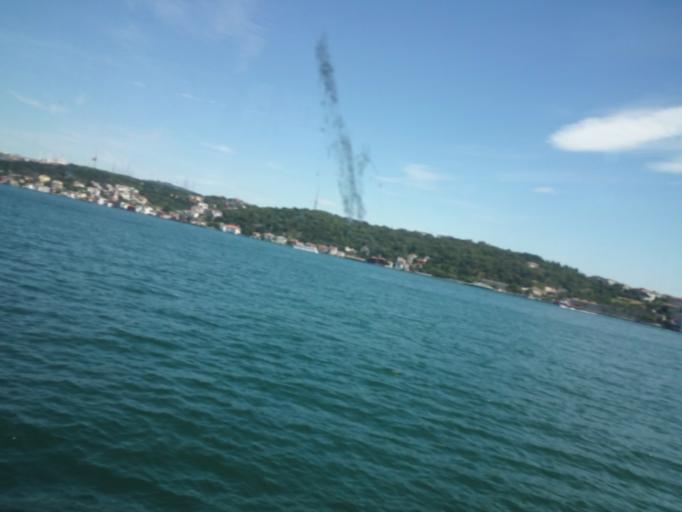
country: TR
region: Istanbul
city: UEskuedar
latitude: 41.0387
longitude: 29.0160
